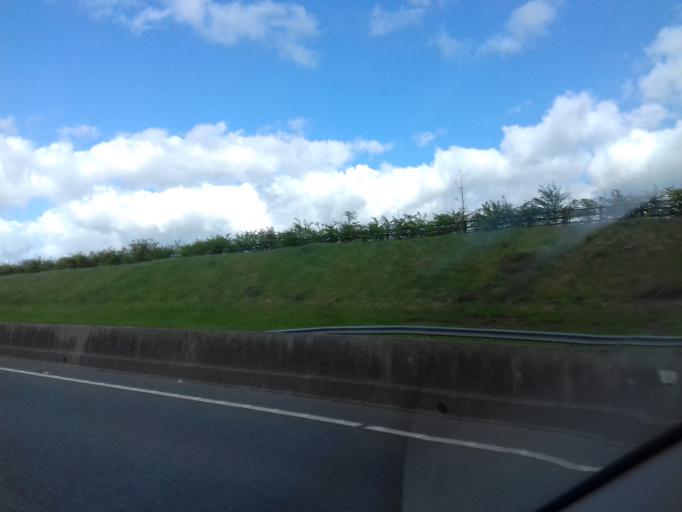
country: IE
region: Leinster
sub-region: Kilkenny
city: Thomastown
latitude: 52.5107
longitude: -7.2408
